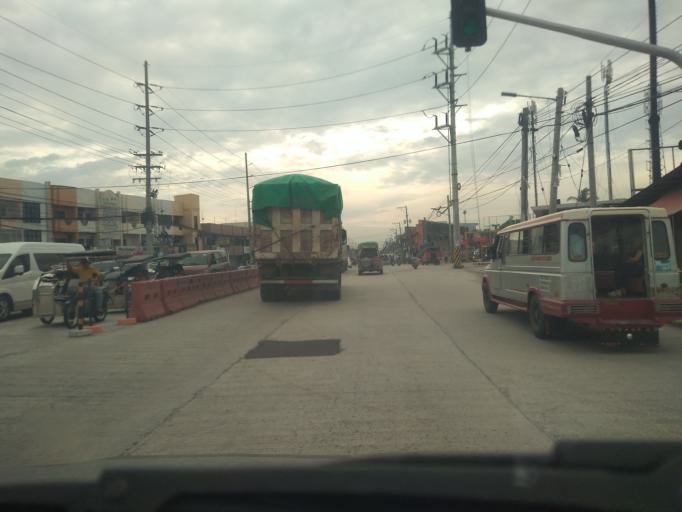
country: PH
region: Central Luzon
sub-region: Province of Pampanga
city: Magliman
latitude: 15.0452
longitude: 120.6718
